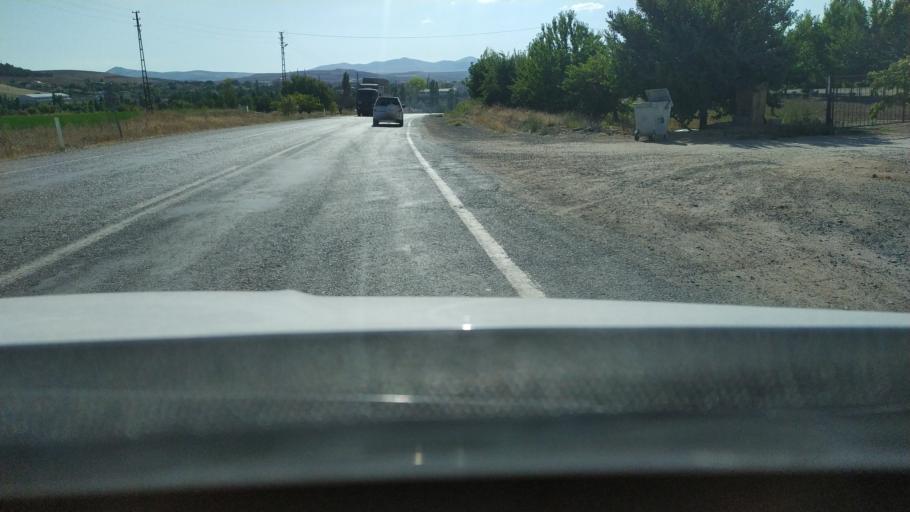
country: TR
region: Kayseri
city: Felahiye
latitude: 39.0964
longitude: 35.5808
